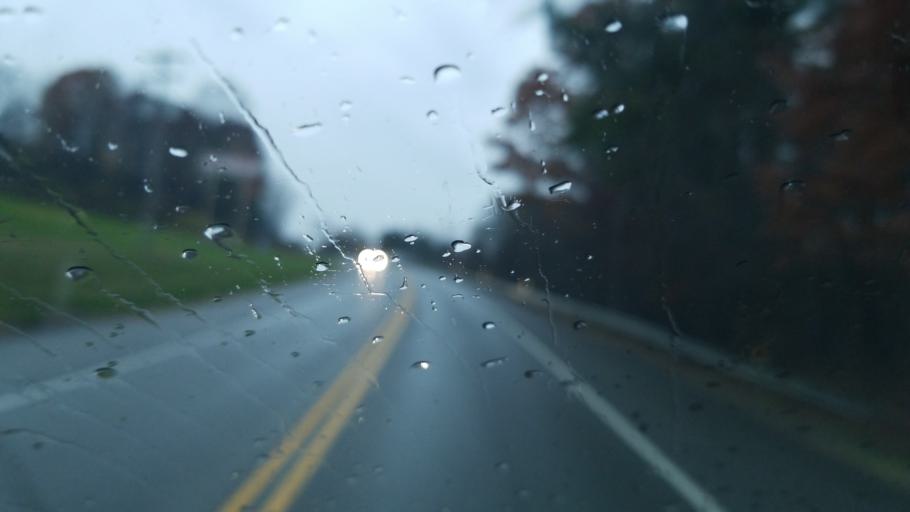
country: US
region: Pennsylvania
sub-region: Clarion County
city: Marianne
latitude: 41.2171
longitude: -79.4354
